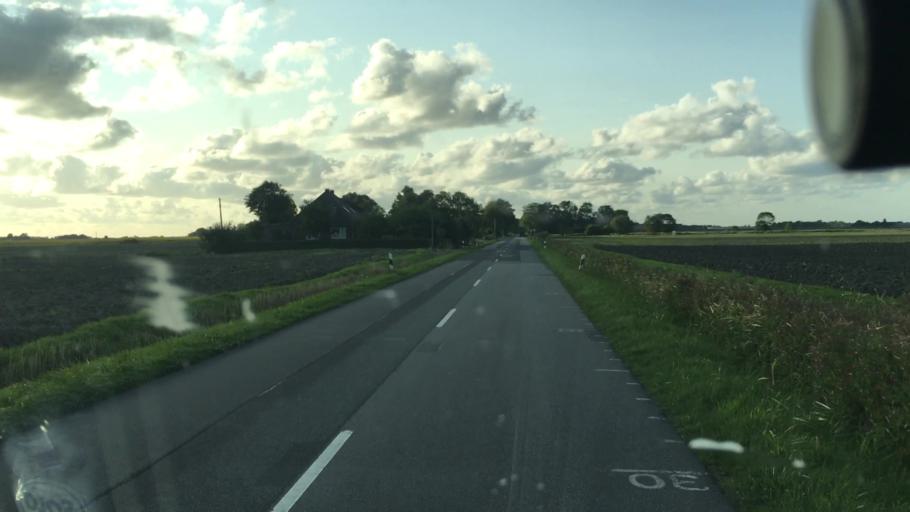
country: DE
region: Lower Saxony
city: Werdum
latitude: 53.6643
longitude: 7.7354
